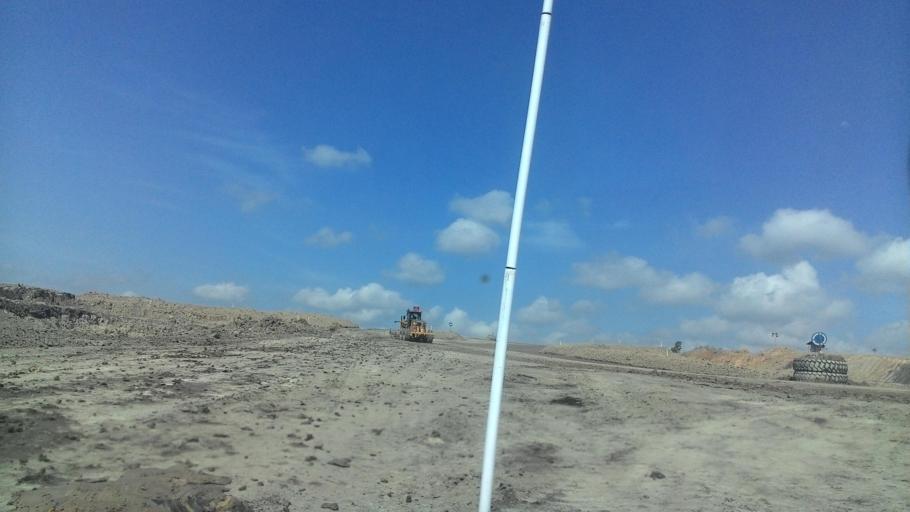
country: ID
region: South Kalimantan
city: Tanta
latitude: -2.1853
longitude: 115.4780
